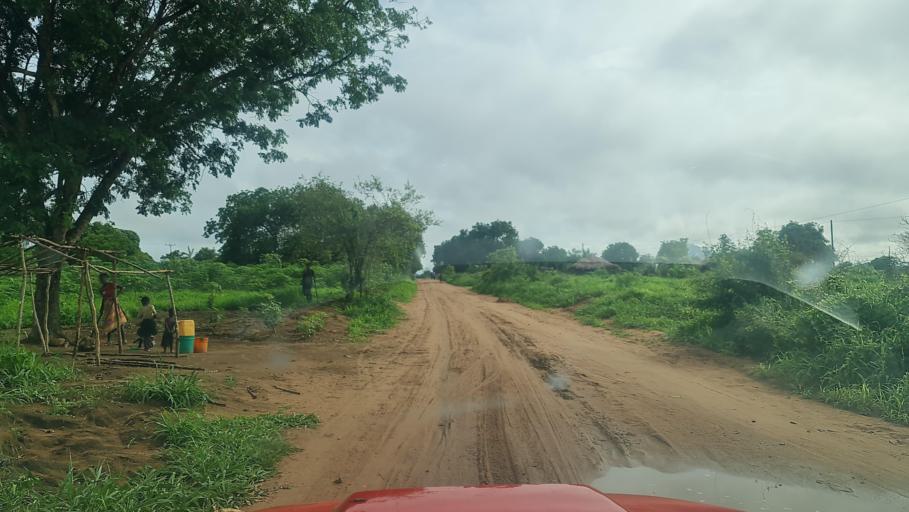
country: MW
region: Southern Region
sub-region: Nsanje District
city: Nsanje
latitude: -17.2845
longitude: 35.6109
